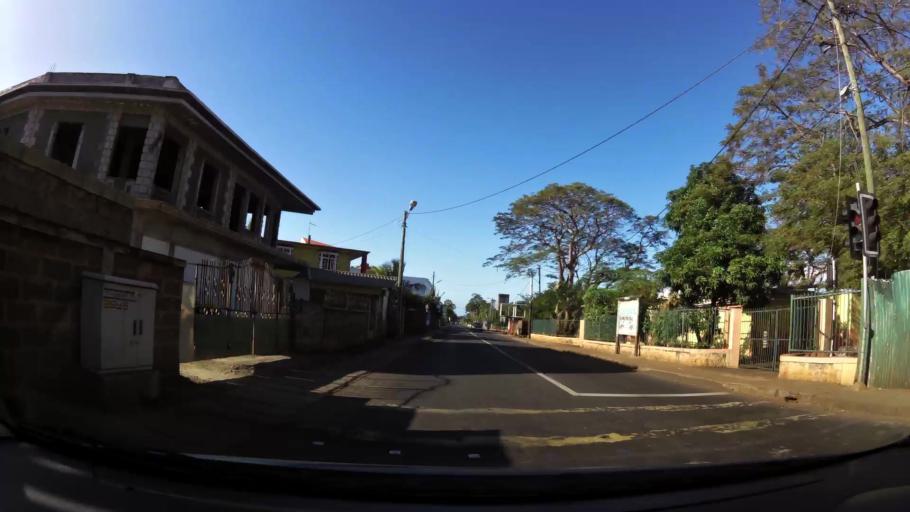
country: MU
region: Black River
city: Petite Riviere
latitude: -20.1942
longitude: 57.4488
